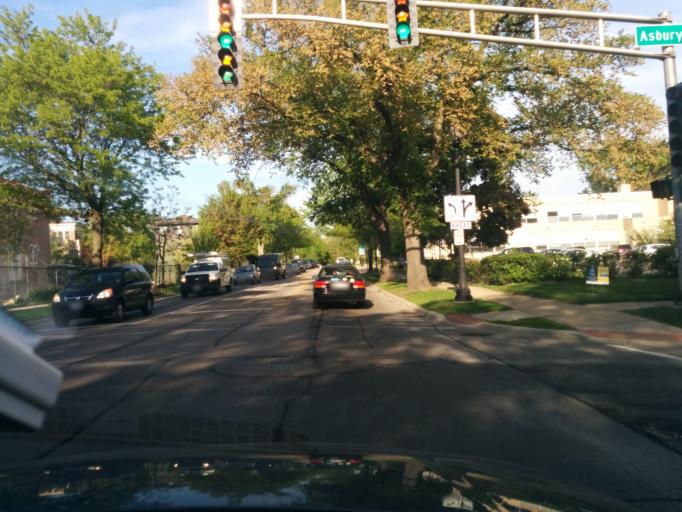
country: US
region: Illinois
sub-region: Cook County
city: Evanston
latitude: 42.0411
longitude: -87.6906
